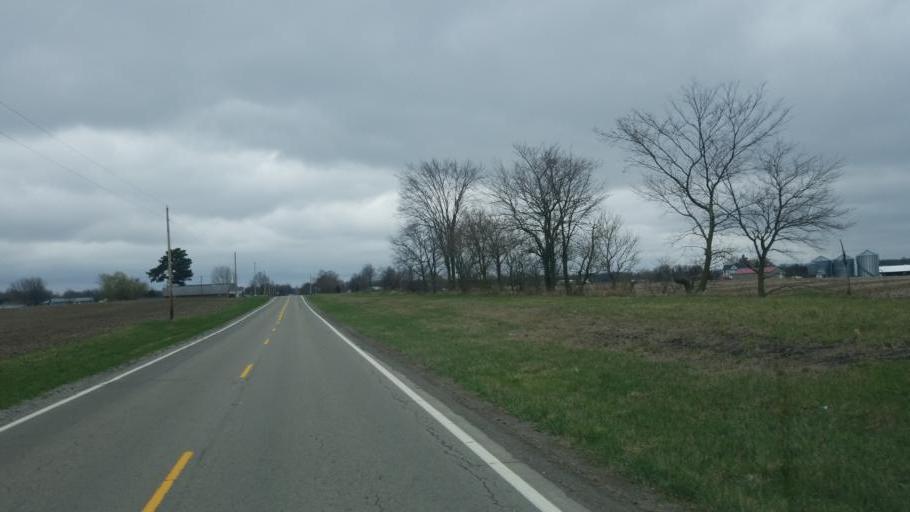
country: US
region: Ohio
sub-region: Hardin County
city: Kenton
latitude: 40.6693
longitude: -83.6000
